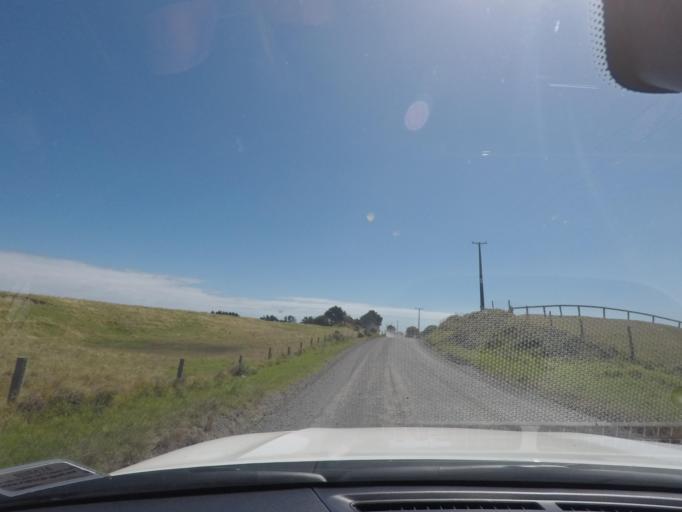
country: NZ
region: Auckland
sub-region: Auckland
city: Parakai
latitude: -36.5853
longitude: 174.2908
